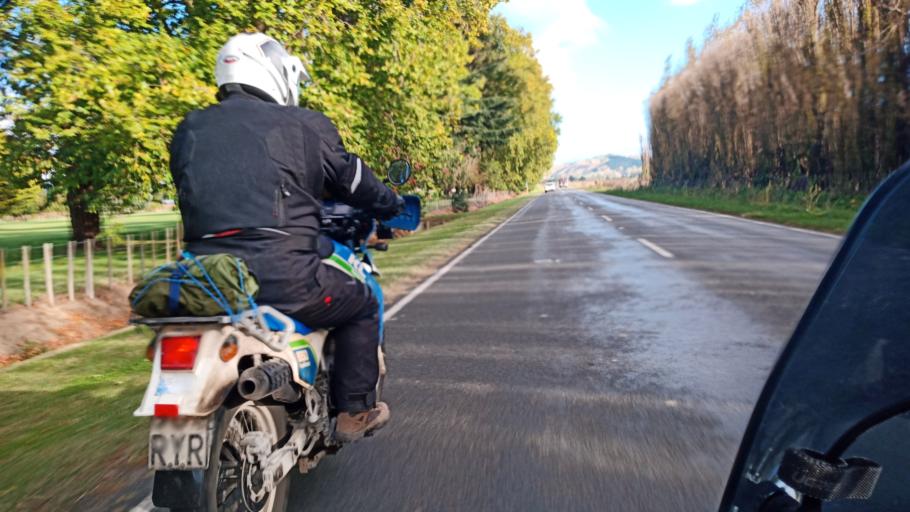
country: NZ
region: Gisborne
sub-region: Gisborne District
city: Gisborne
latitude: -38.6374
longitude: 177.9113
